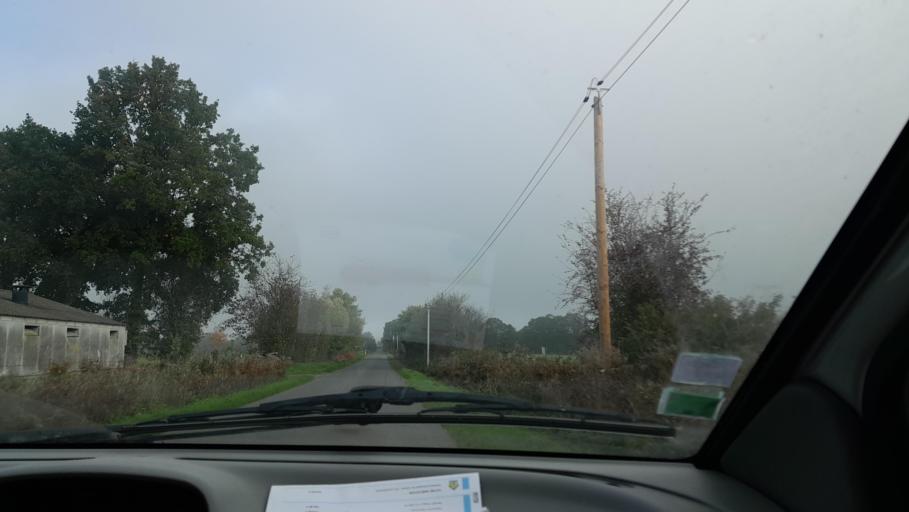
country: FR
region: Pays de la Loire
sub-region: Departement de la Mayenne
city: Saint-Pierre-la-Cour
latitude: 48.1496
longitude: -1.0326
